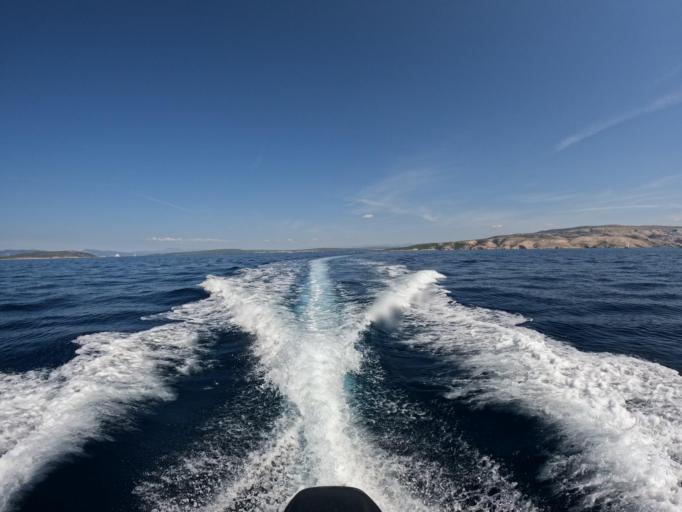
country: HR
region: Primorsko-Goranska
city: Punat
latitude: 44.9367
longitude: 14.6162
